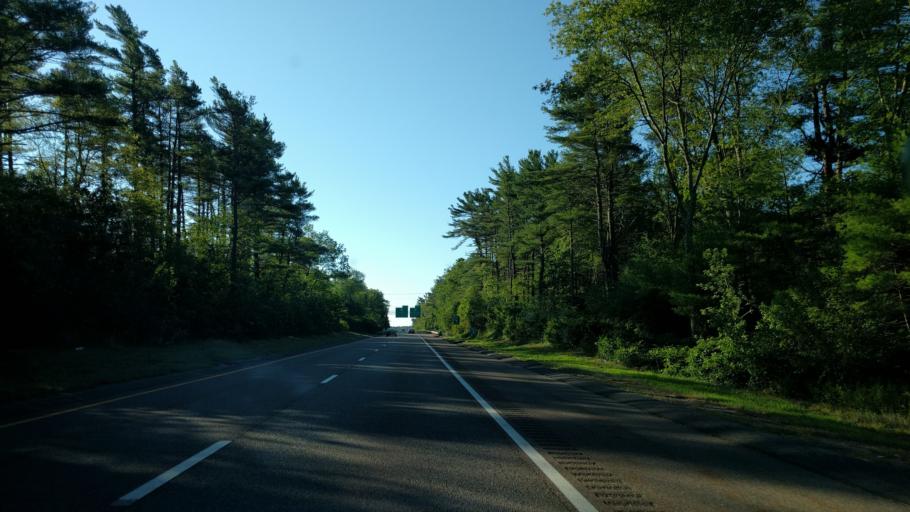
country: US
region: Massachusetts
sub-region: Plymouth County
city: Middleborough Center
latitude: 41.9094
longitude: -70.9756
